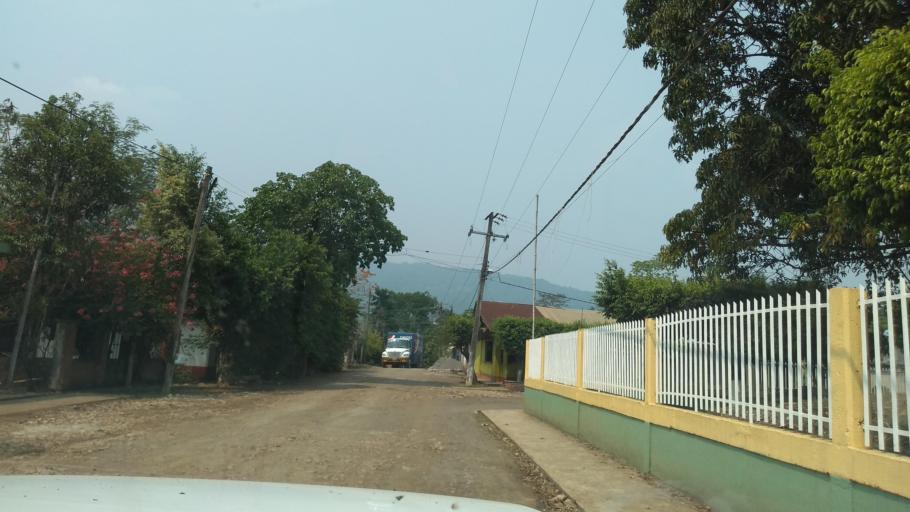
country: MX
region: Veracruz
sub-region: Tezonapa
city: Laguna Chica (Pueblo Nuevo)
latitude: 18.5443
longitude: -96.7768
